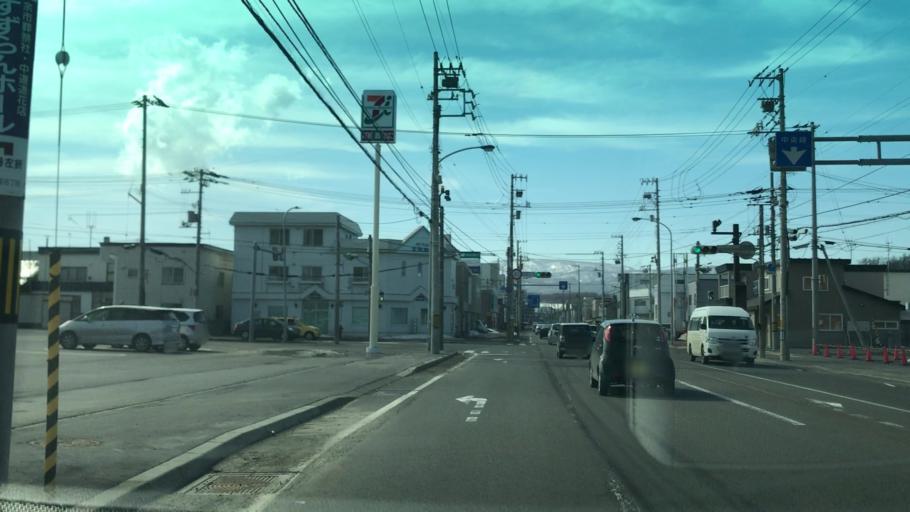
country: JP
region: Hokkaido
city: Yoichi
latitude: 43.1924
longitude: 140.8006
